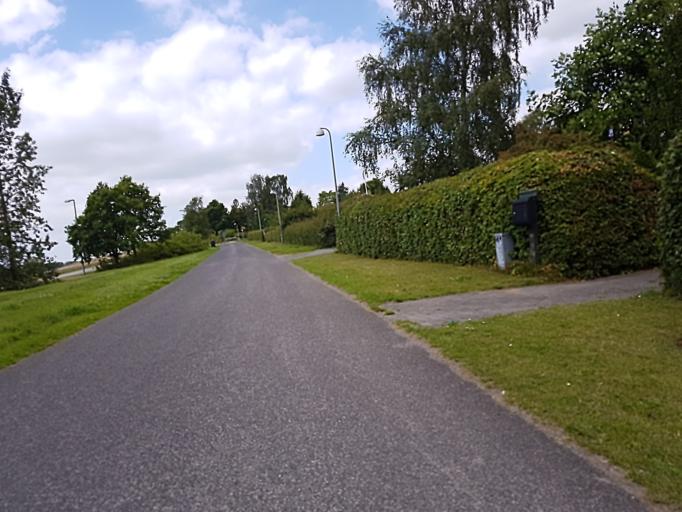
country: DK
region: Capital Region
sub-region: Ballerup Kommune
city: Malov
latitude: 55.7884
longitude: 12.3181
